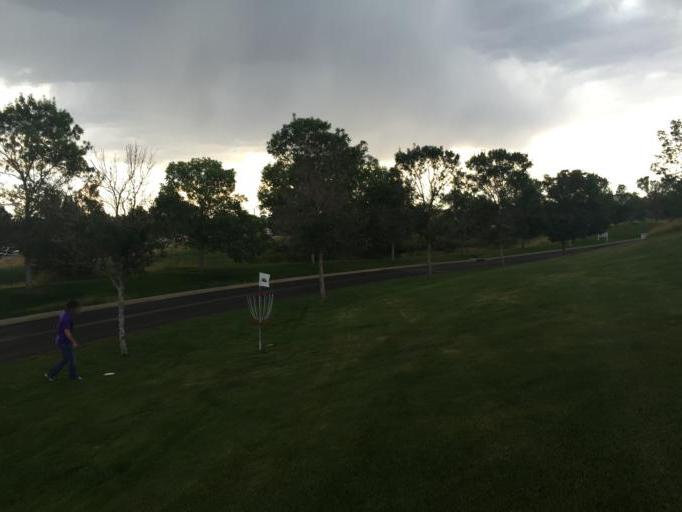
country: US
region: Colorado
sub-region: Adams County
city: Northglenn
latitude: 39.9132
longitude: -104.9994
